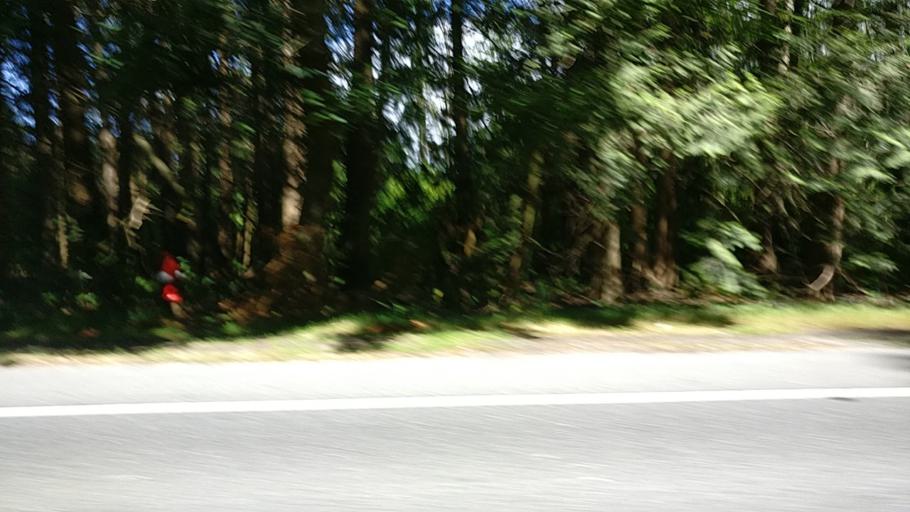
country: CA
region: British Columbia
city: Surrey
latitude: 49.0646
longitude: -122.8409
